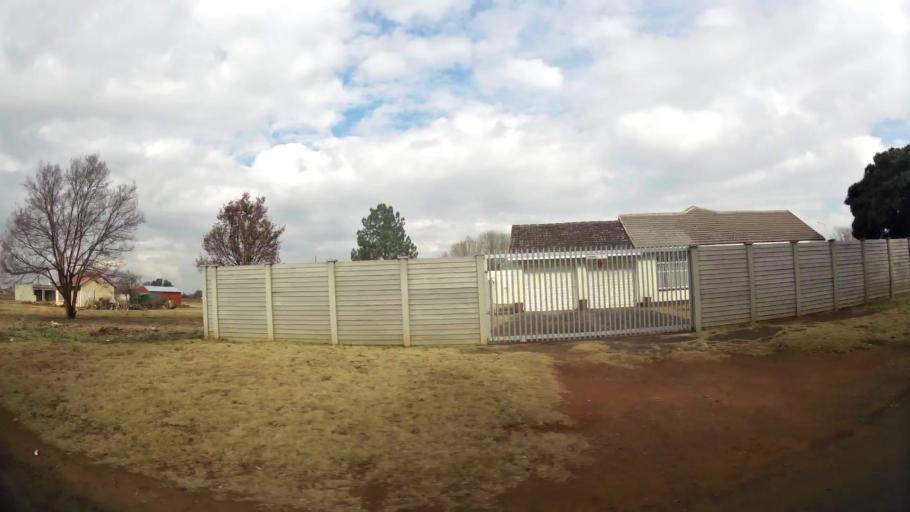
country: ZA
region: Gauteng
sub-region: Sedibeng District Municipality
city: Meyerton
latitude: -26.5898
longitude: 28.0027
